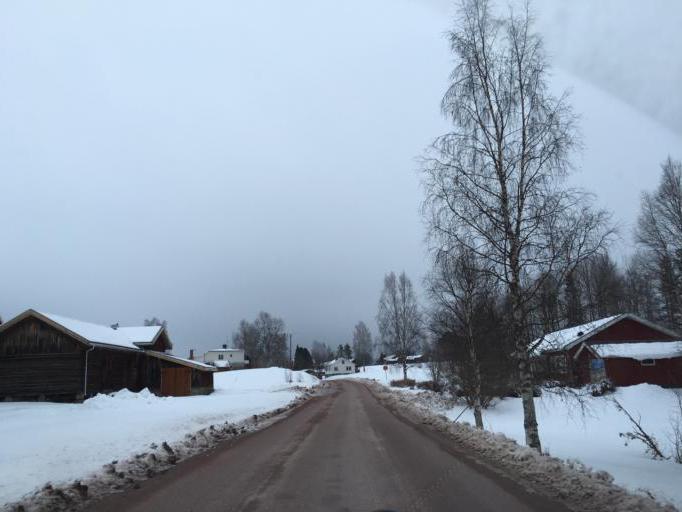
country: SE
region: Dalarna
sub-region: Alvdalens Kommun
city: AElvdalen
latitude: 61.2566
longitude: 14.0592
